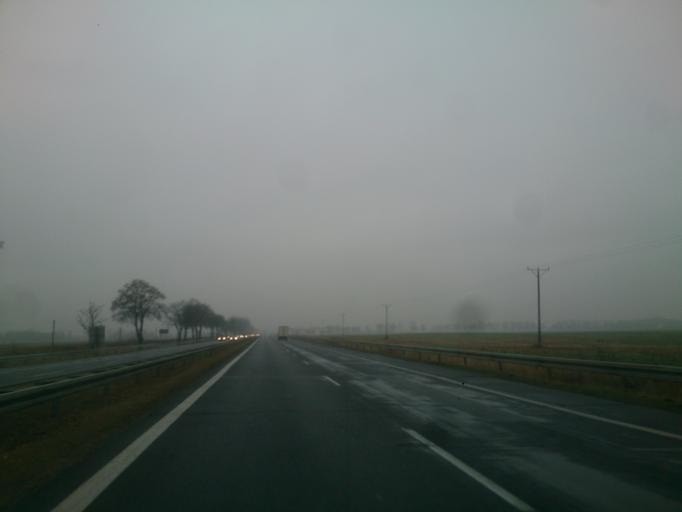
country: PL
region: Masovian Voivodeship
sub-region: Powiat warszawski zachodni
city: Dziekanow Lesny
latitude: 52.3671
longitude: 20.8058
